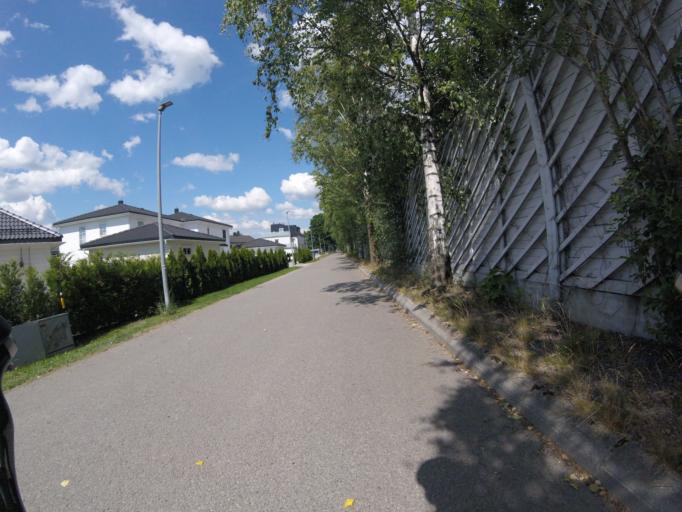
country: NO
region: Akershus
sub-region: Skedsmo
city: Lillestrom
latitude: 59.9569
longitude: 11.0707
